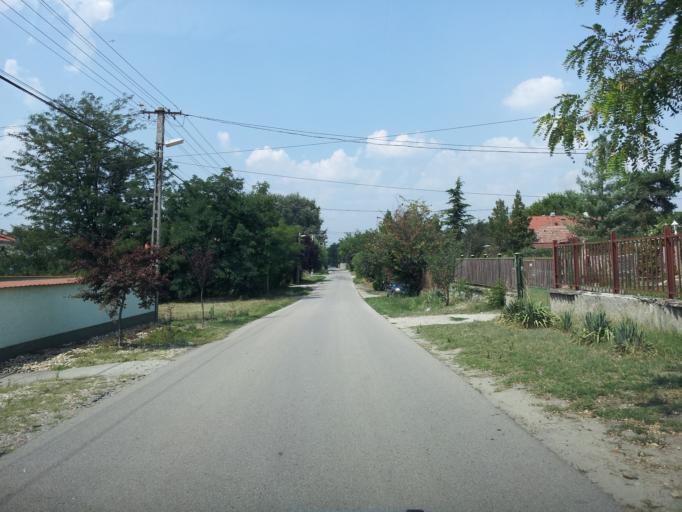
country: HU
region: Pest
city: Szigethalom
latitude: 47.3159
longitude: 19.0200
